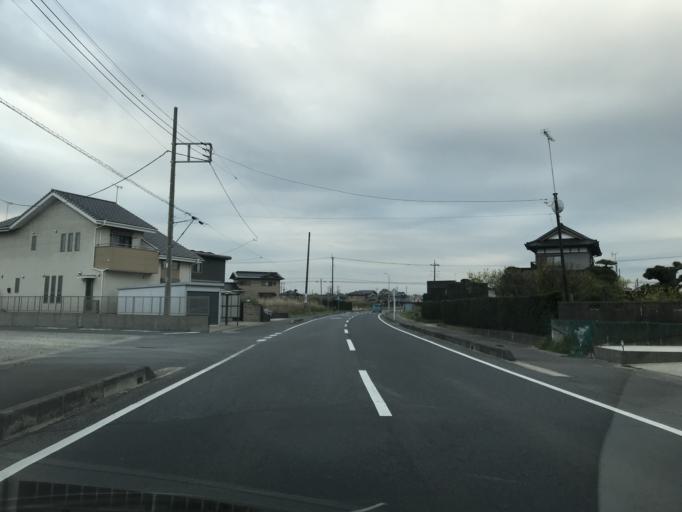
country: JP
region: Ibaraki
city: Kashima-shi
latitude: 35.9156
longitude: 140.6287
